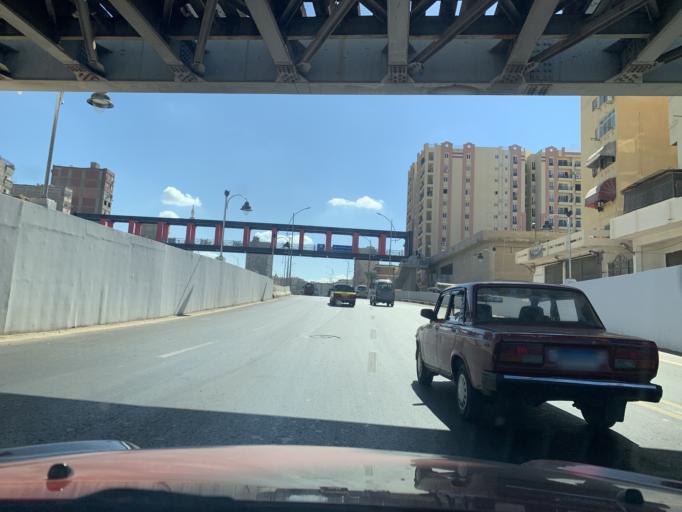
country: EG
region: Alexandria
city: Alexandria
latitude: 31.2170
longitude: 29.9632
